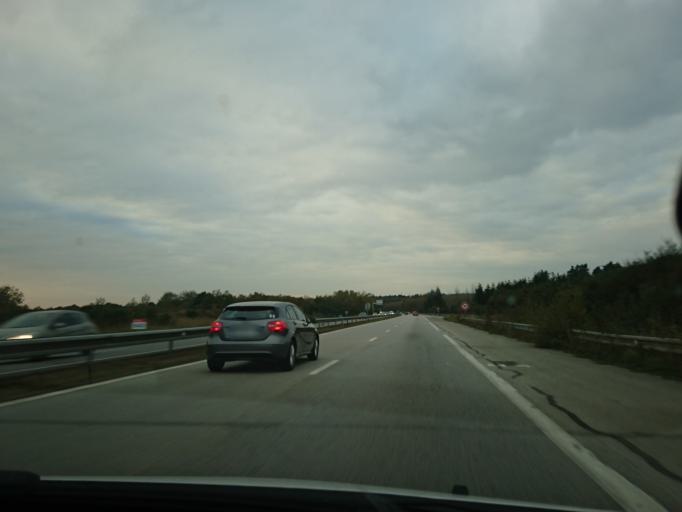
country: FR
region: Brittany
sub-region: Departement du Morbihan
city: Branderion
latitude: 47.7796
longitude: -3.1983
